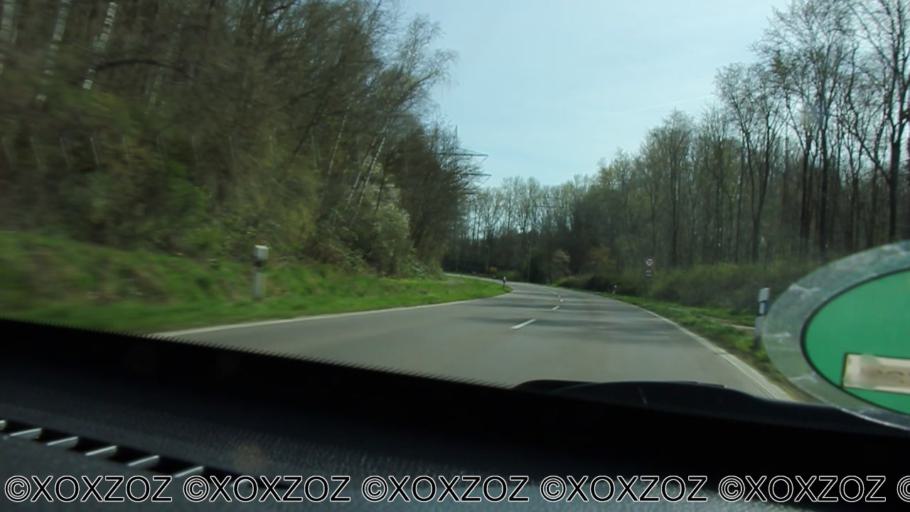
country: DE
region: North Rhine-Westphalia
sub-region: Regierungsbezirk Koln
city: Bedburg
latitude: 51.0387
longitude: 6.6019
